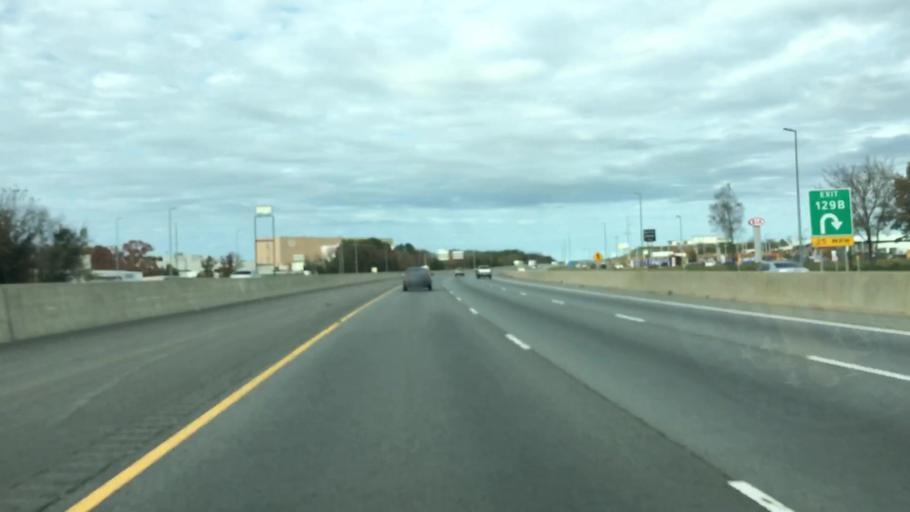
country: US
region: Arkansas
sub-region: Faulkner County
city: Conway
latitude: 35.0674
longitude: -92.4177
